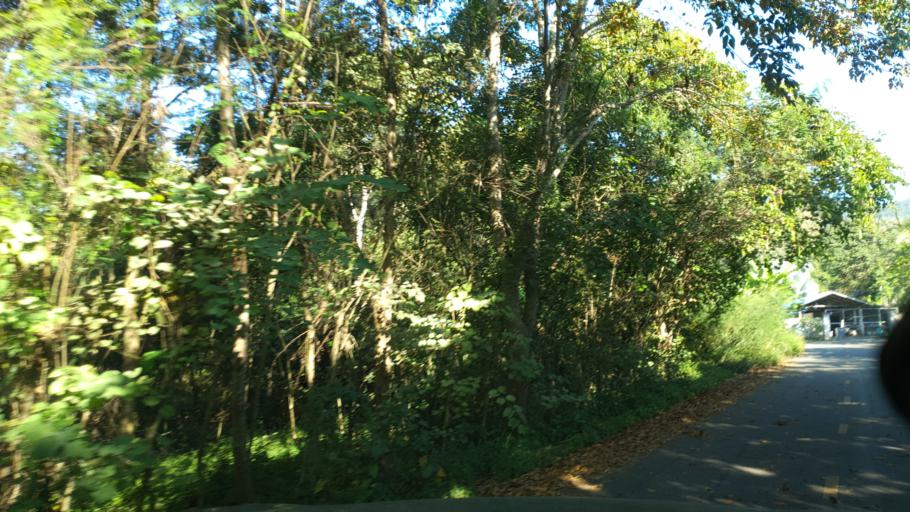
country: TH
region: Chiang Mai
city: Mae On
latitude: 18.7464
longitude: 99.2150
